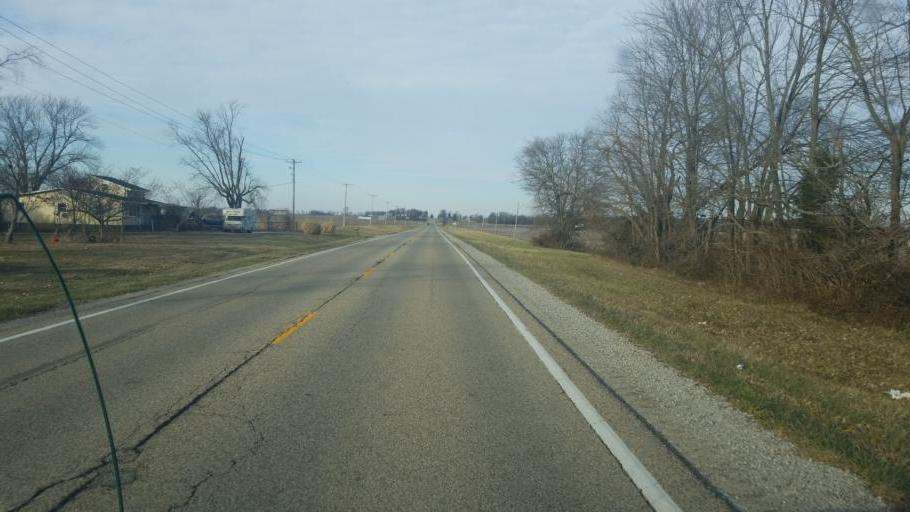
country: US
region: Illinois
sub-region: Lawrence County
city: Bridgeport
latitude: 38.5982
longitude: -87.6943
